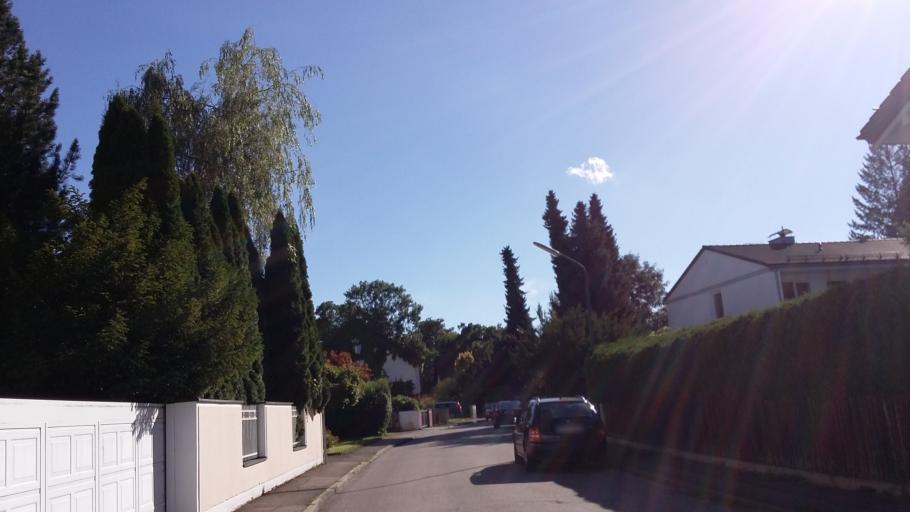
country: DE
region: Bavaria
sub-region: Upper Bavaria
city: Planegg
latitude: 48.0941
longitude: 11.4088
